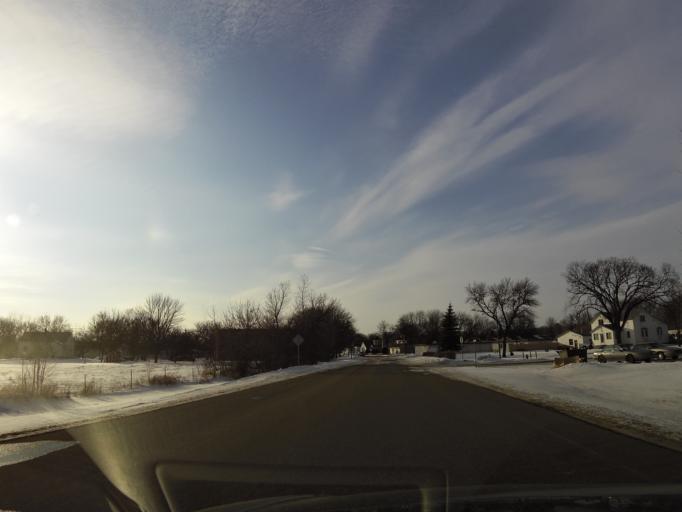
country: US
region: North Dakota
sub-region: Walsh County
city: Grafton
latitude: 48.4189
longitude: -97.3974
